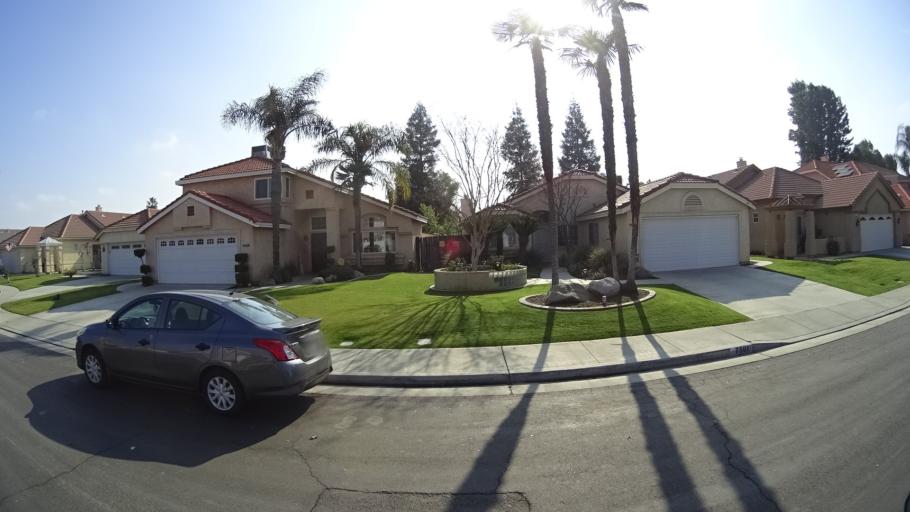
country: US
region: California
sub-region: Kern County
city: Greenacres
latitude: 35.3038
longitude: -119.0861
